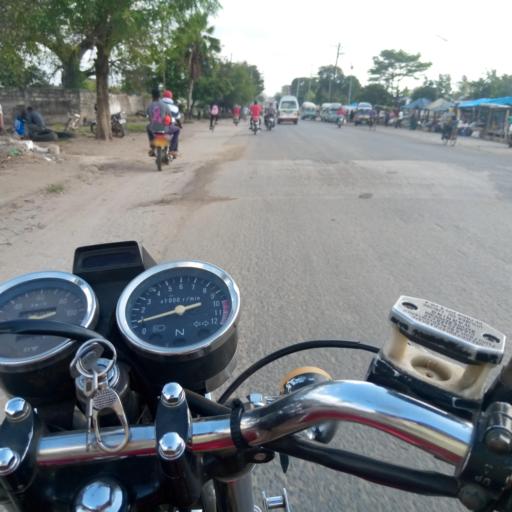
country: TZ
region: Tanga
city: Tanga
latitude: -5.0894
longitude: 39.0967
